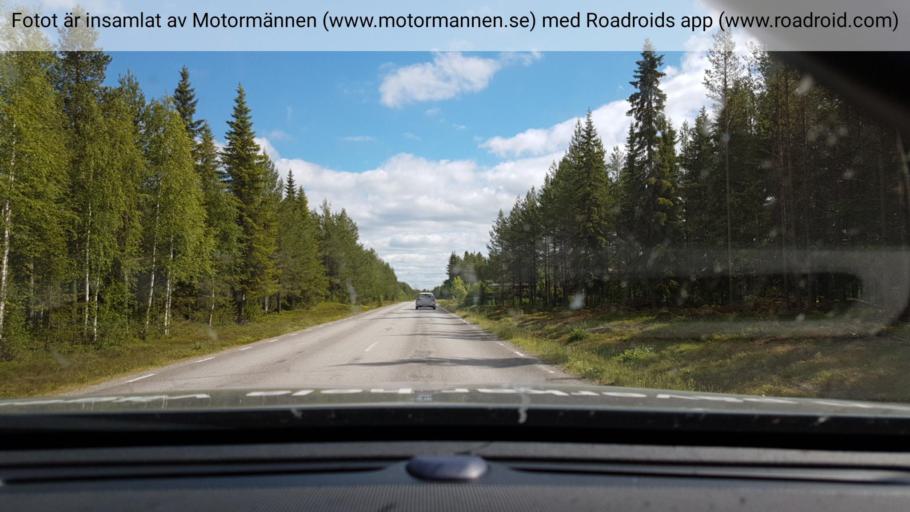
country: SE
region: Vaesterbotten
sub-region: Sorsele Kommun
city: Sorsele
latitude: 65.5979
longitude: 17.4977
